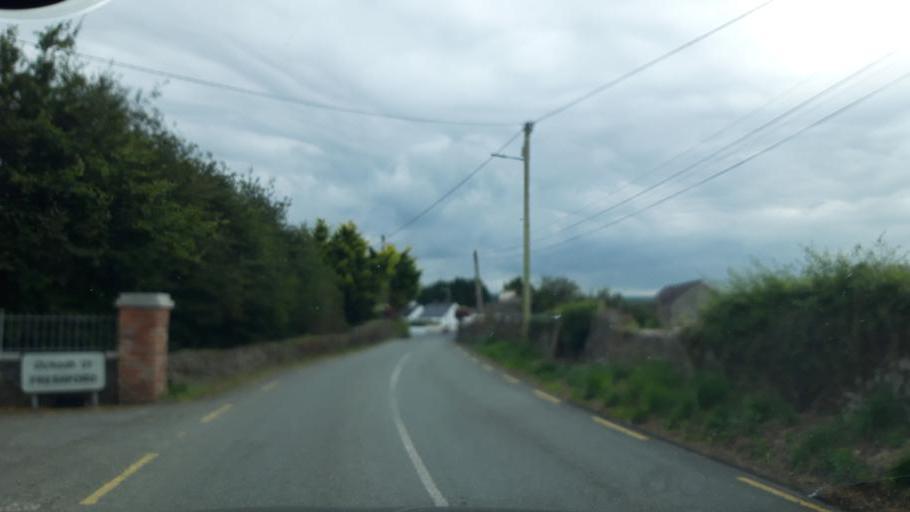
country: IE
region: Leinster
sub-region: Kilkenny
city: Ballyragget
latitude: 52.7385
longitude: -7.3981
